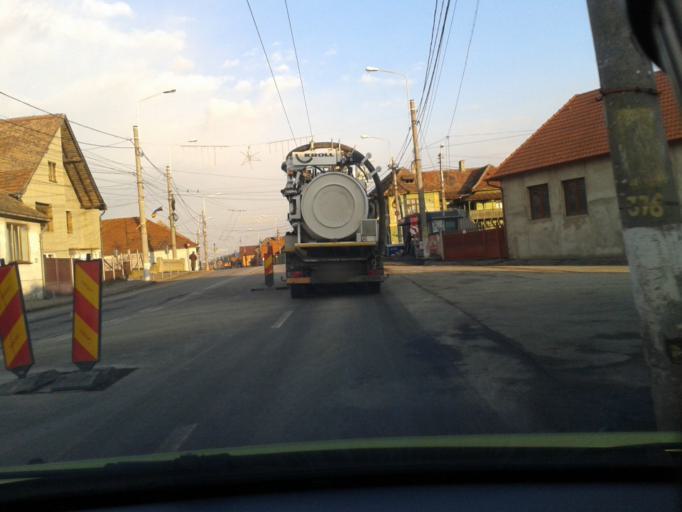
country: RO
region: Sibiu
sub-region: Municipiul Medias
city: Medias
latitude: 46.1655
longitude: 24.3596
